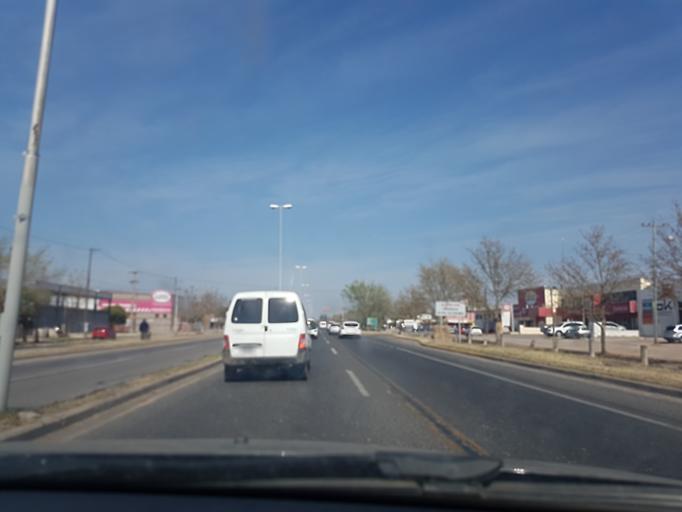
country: AR
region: Cordoba
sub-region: Departamento de Capital
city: Cordoba
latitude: -31.4787
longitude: -64.2383
